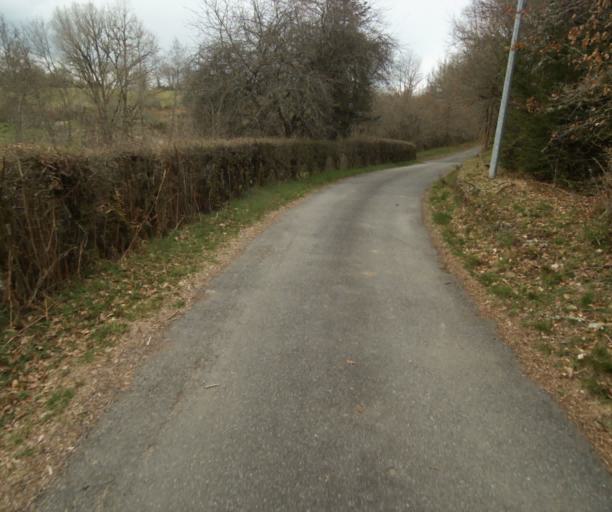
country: FR
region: Limousin
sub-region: Departement de la Correze
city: Correze
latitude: 45.3132
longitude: 1.8907
